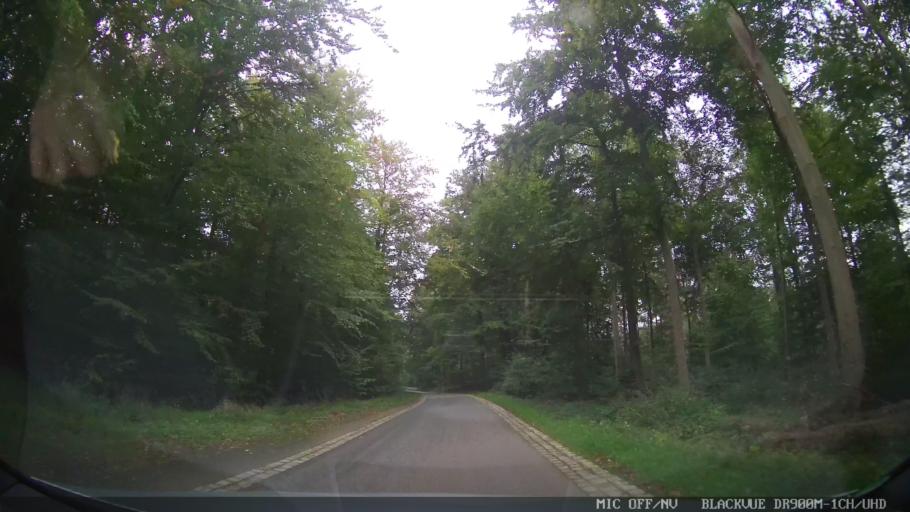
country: DE
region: Schleswig-Holstein
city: Gromitz
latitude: 54.1825
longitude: 10.9729
